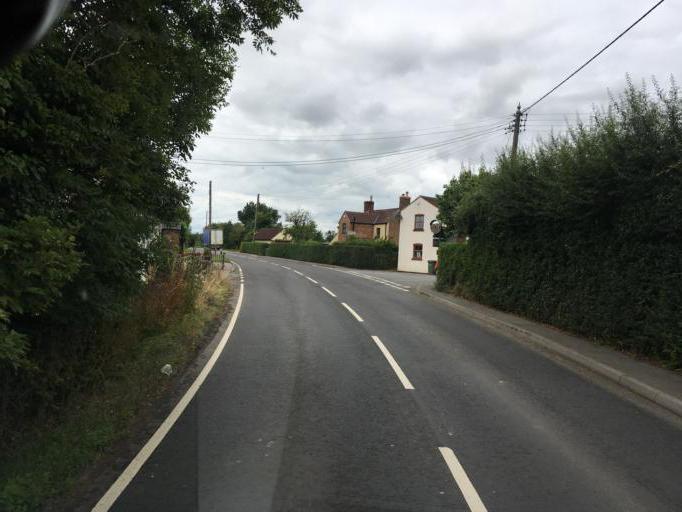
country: GB
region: England
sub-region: Gloucestershire
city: Stonehouse
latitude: 51.7419
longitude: -2.3232
